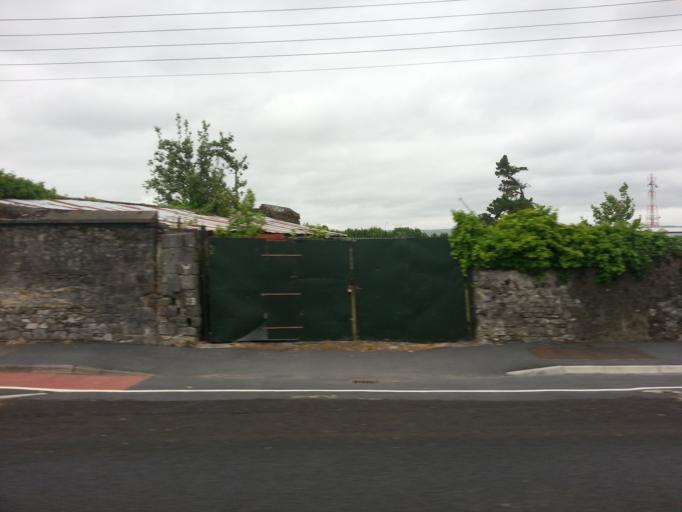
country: IE
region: Leinster
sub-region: Kilkenny
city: Kilkenny
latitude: 52.6511
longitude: -7.2356
